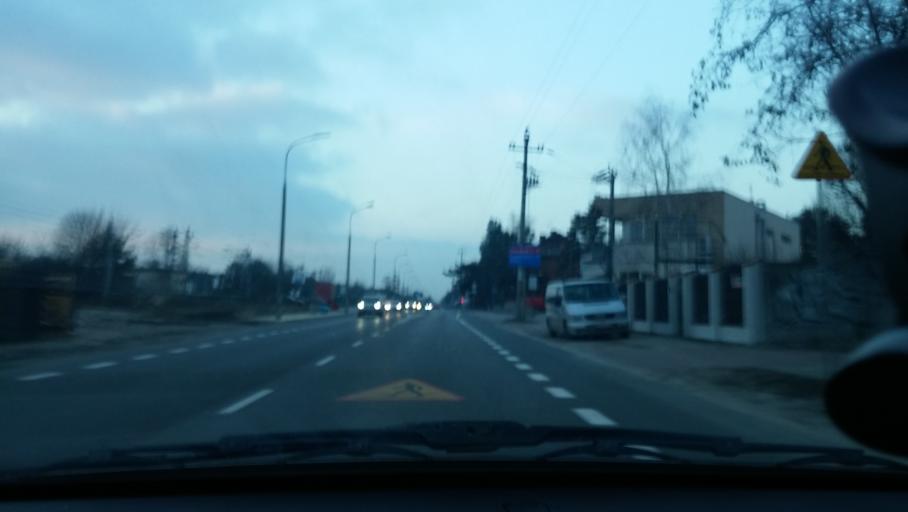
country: PL
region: Masovian Voivodeship
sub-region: Warszawa
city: Wawer
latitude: 52.1913
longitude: 21.1822
